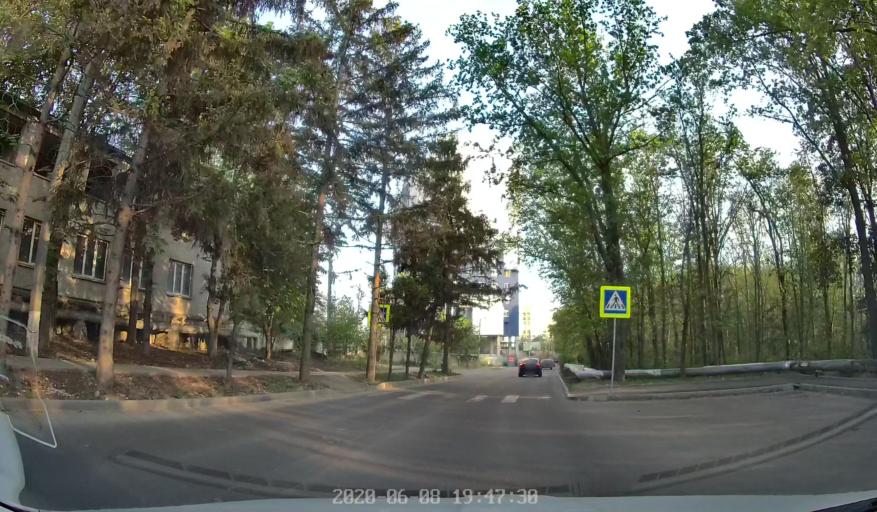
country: MD
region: Chisinau
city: Stauceni
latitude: 47.0592
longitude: 28.8869
